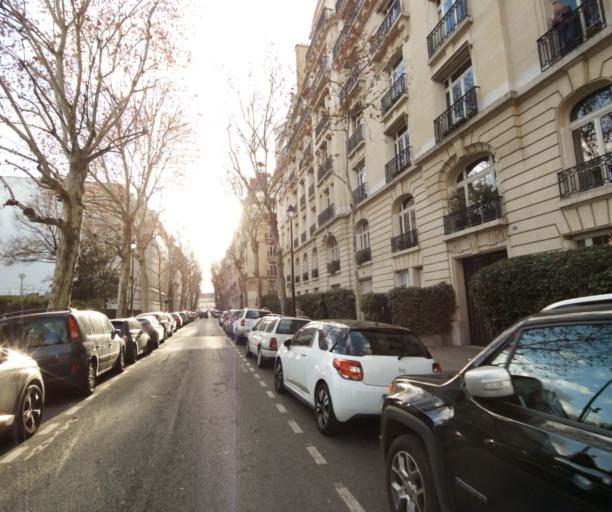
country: FR
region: Ile-de-France
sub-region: Departement des Hauts-de-Seine
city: Neuilly-sur-Seine
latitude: 48.8836
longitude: 2.2813
